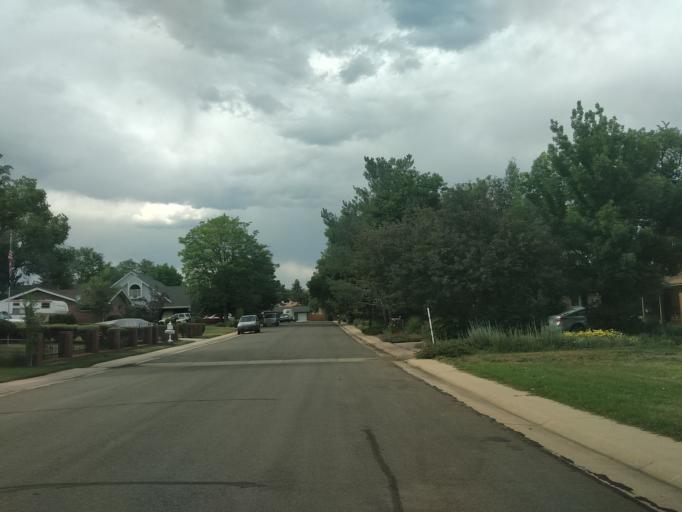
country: US
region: Colorado
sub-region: Jefferson County
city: Lakewood
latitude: 39.7016
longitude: -105.0957
